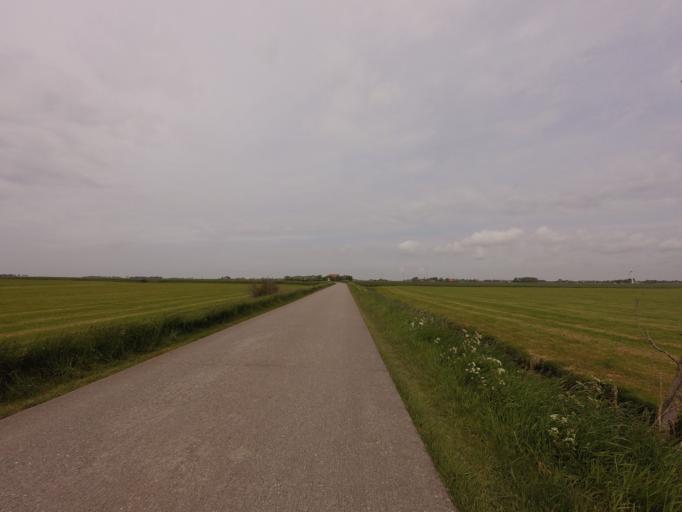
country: NL
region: Friesland
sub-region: Sudwest Fryslan
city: Makkum
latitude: 53.0665
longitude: 5.4586
